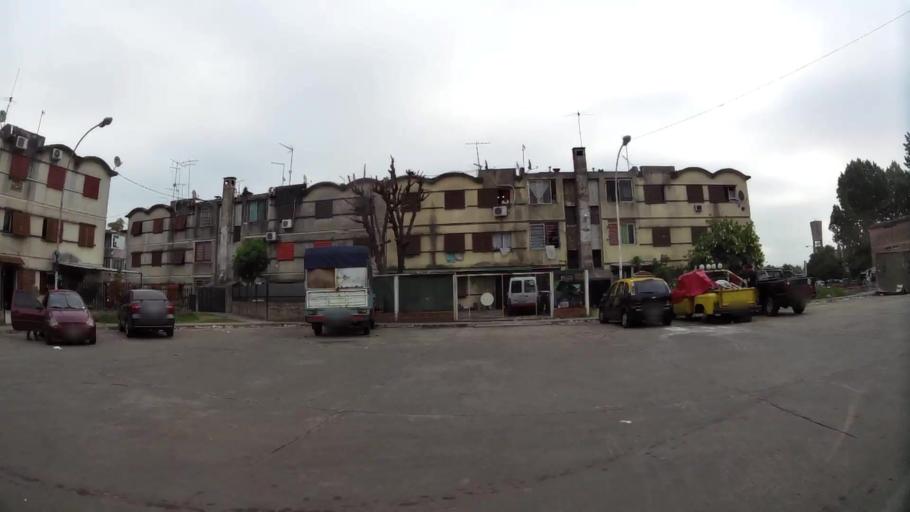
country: AR
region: Buenos Aires
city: San Justo
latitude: -34.6937
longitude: -58.5747
